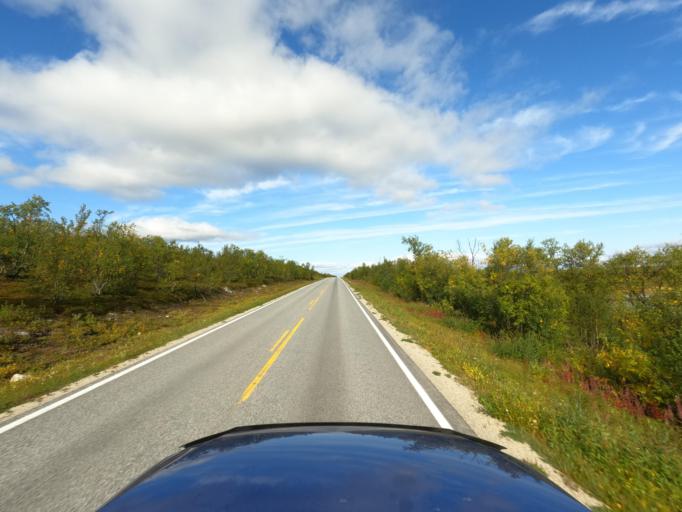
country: NO
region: Finnmark Fylke
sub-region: Karasjok
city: Karasjohka
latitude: 69.6512
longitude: 25.2793
